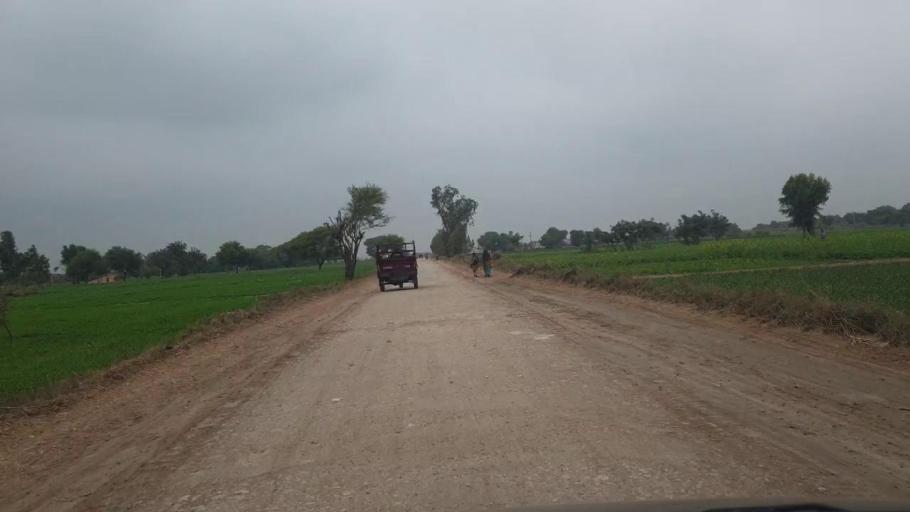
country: PK
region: Sindh
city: Shahdadpur
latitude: 25.9425
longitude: 68.7251
